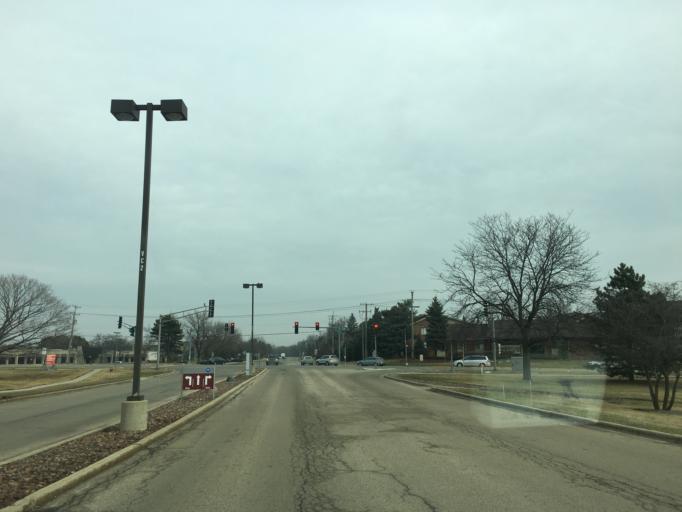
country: US
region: Illinois
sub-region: Cook County
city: Hoffman Estates
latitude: 42.0708
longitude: -88.0535
